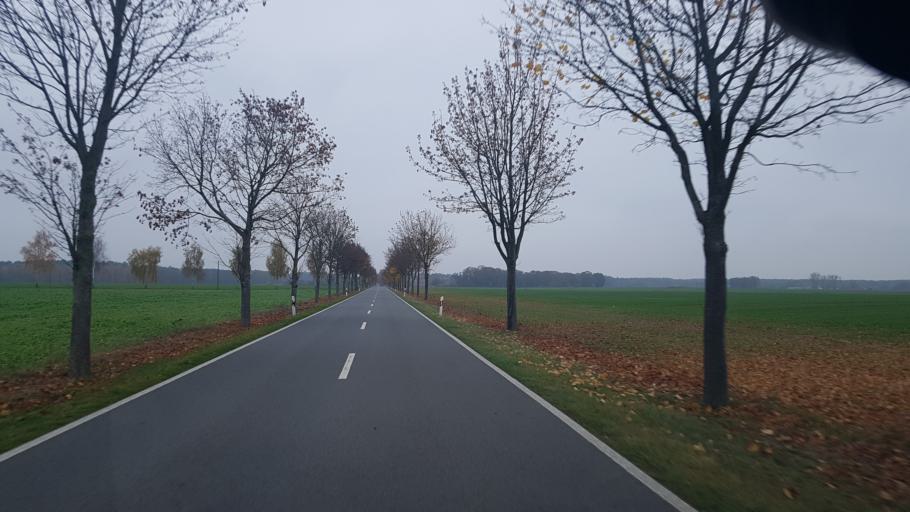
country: DE
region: Brandenburg
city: Lindow
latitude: 52.9437
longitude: 13.0136
